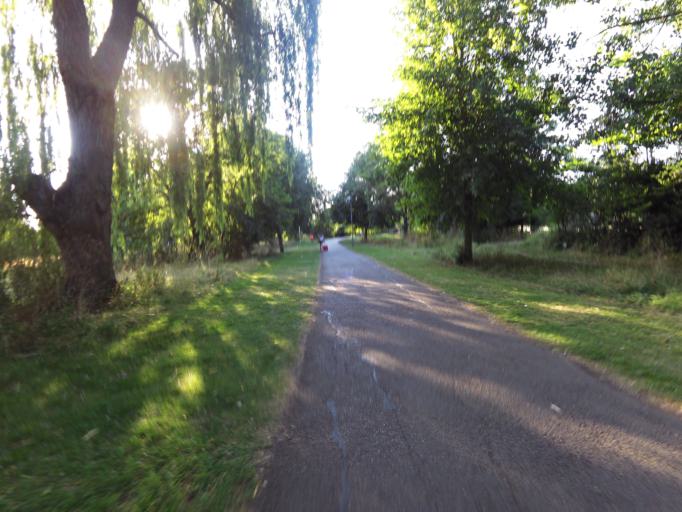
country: GB
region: England
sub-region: Essex
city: Chelmsford
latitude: 51.7381
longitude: 0.4529
